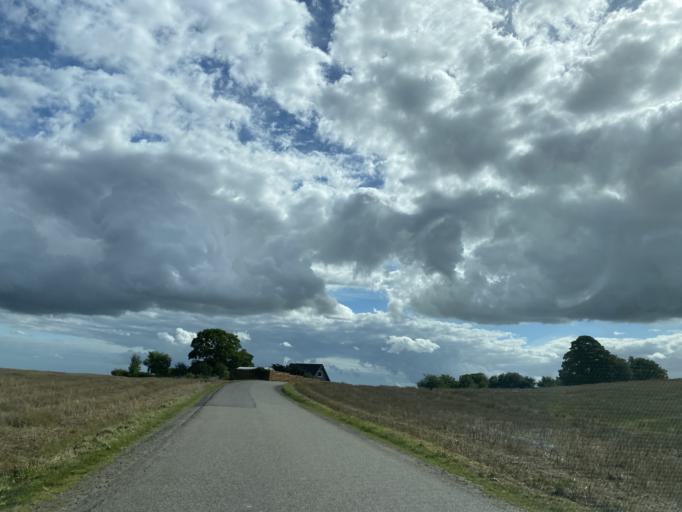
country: DK
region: Central Jutland
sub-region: Skanderborg Kommune
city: Skanderborg
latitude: 55.9761
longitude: 9.8559
